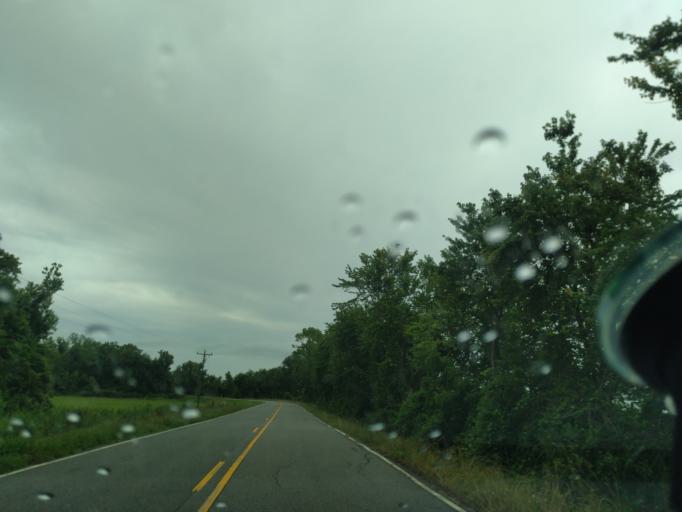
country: US
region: North Carolina
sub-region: Washington County
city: Plymouth
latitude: 35.7746
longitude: -76.5268
